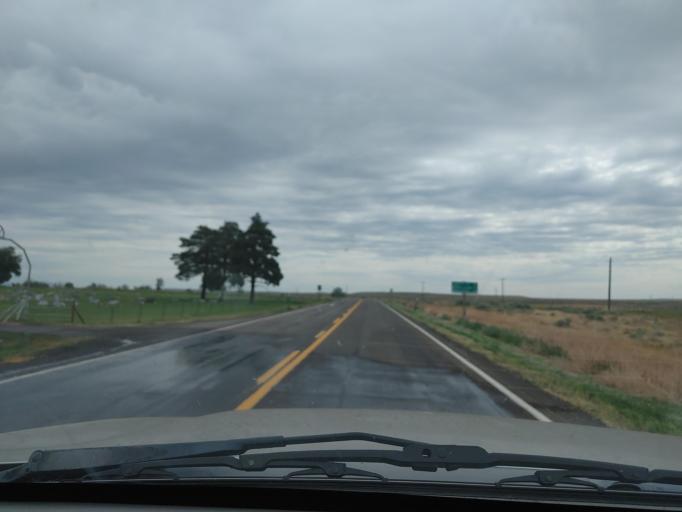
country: US
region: Idaho
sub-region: Lincoln County
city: Shoshone
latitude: 43.0495
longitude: -114.1463
